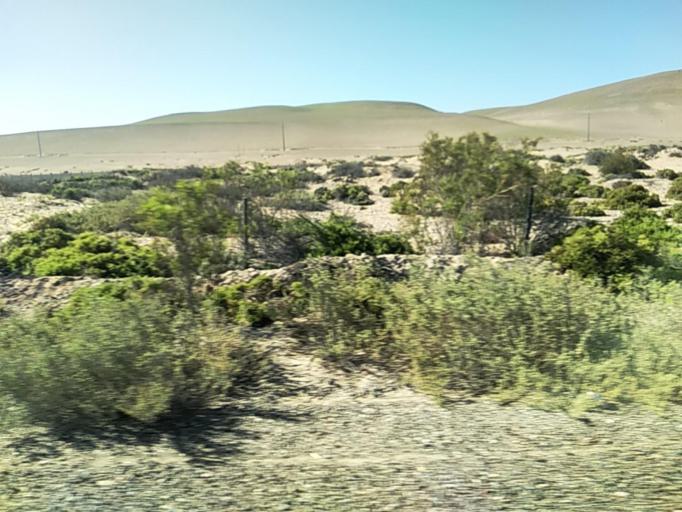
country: CL
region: Atacama
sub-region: Provincia de Copiapo
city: Copiapo
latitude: -27.3463
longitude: -70.7401
